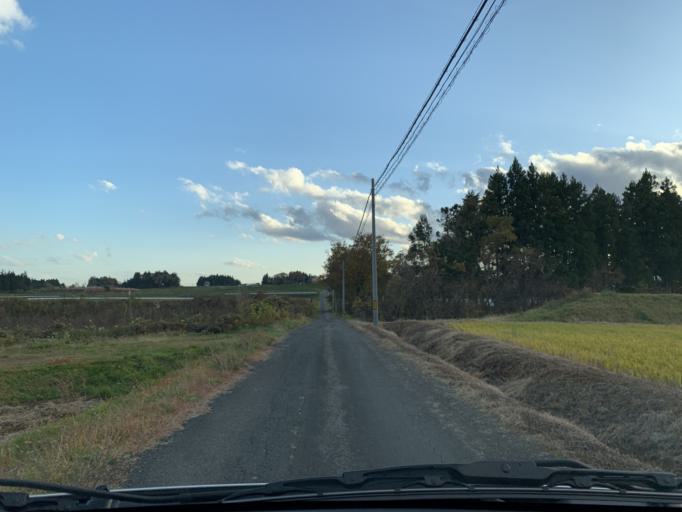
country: JP
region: Iwate
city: Mizusawa
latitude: 39.0972
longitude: 141.0391
